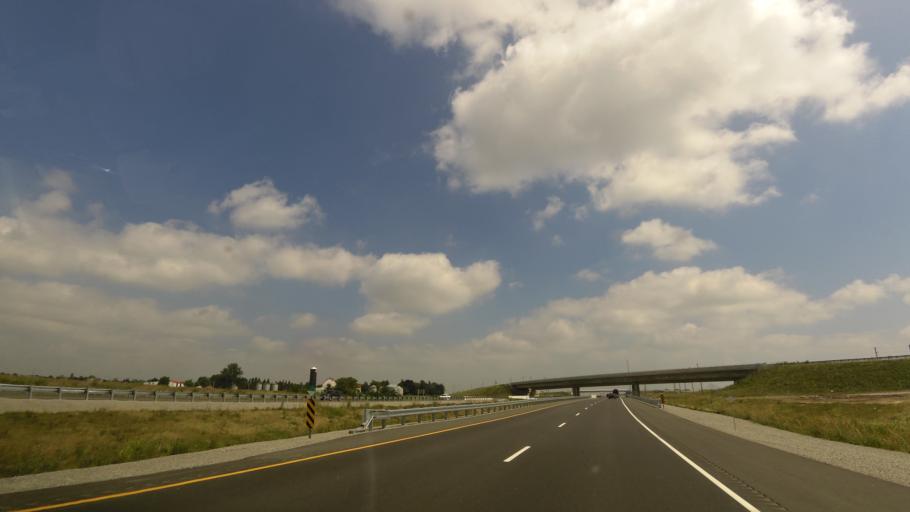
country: CA
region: Ontario
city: Ajax
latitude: 43.9507
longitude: -78.9809
